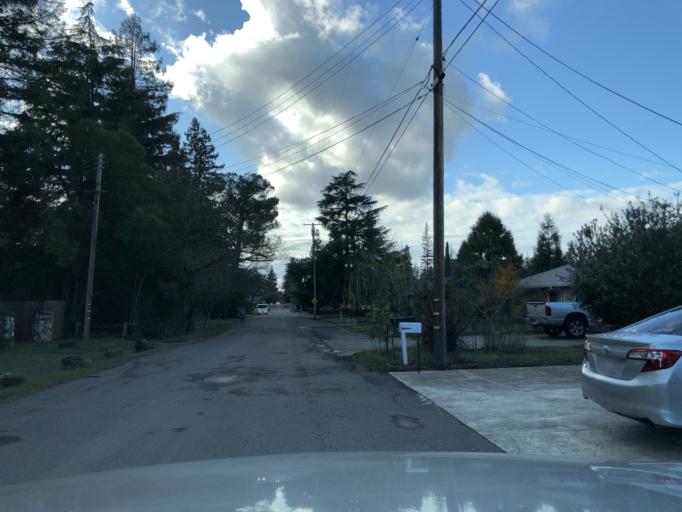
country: US
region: California
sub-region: Sacramento County
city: Foothill Farms
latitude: 38.6561
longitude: -121.3246
